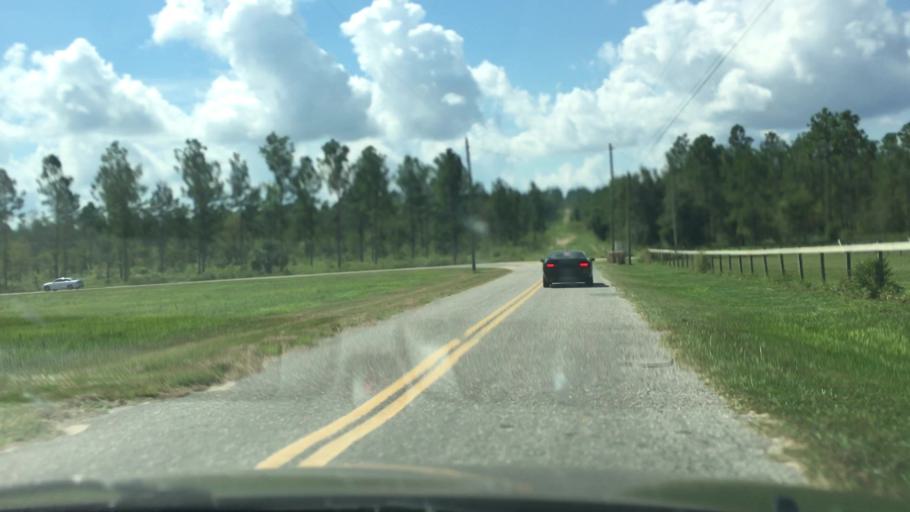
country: US
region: Florida
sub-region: Lake County
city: Minneola
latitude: 28.6384
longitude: -81.7311
